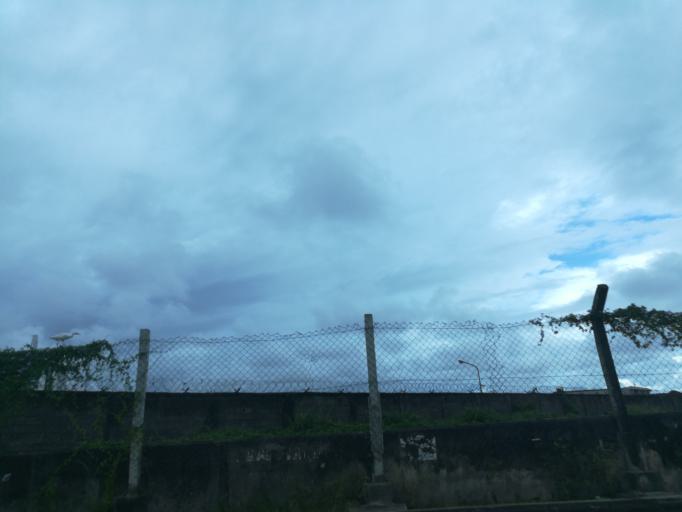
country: NG
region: Lagos
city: Ikoyi
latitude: 6.4447
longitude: 3.4690
